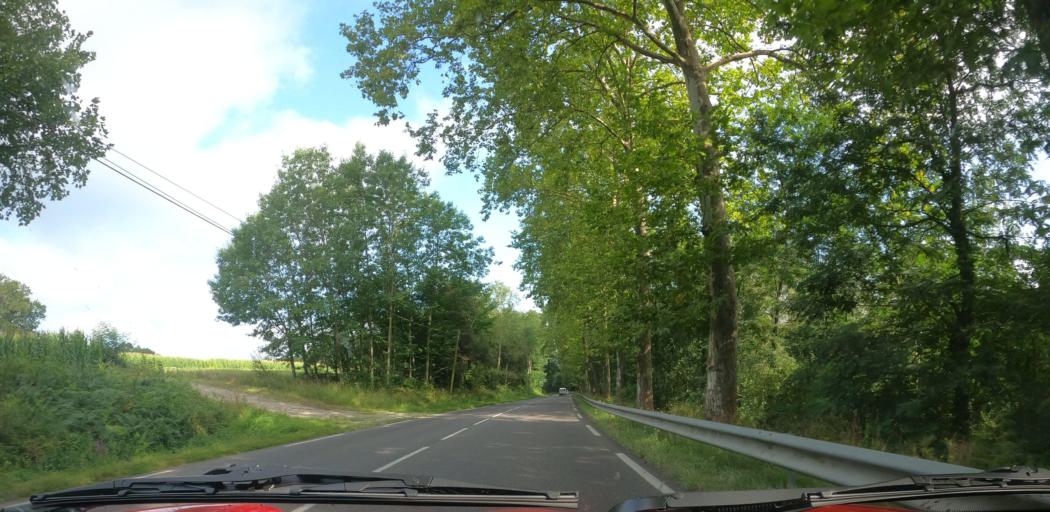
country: FR
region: Aquitaine
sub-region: Departement des Landes
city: Peyrehorade
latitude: 43.5280
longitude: -1.1050
